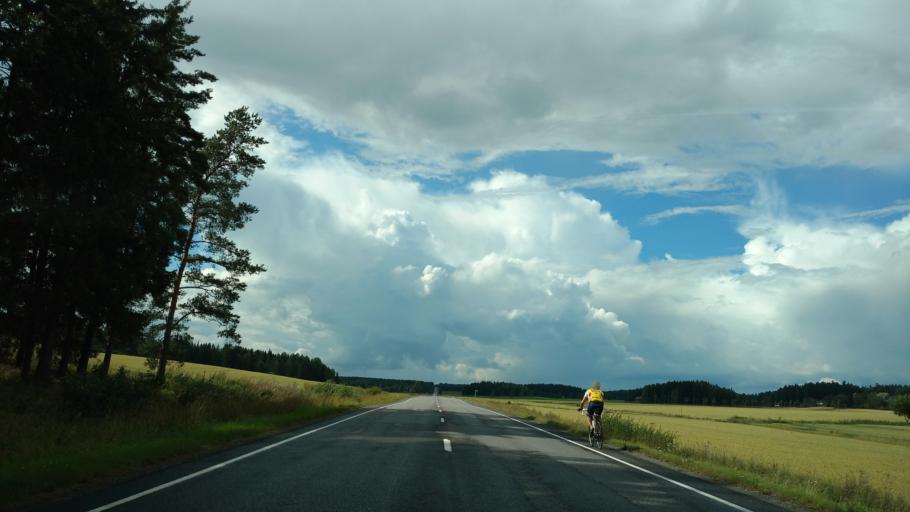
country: FI
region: Varsinais-Suomi
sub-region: Turku
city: Sauvo
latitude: 60.3889
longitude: 22.8763
